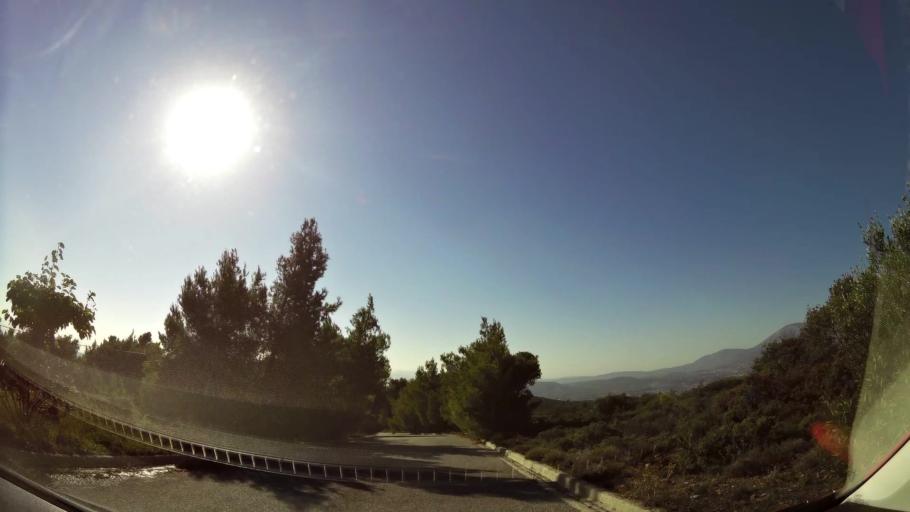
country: GR
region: Attica
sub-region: Nomarchia Anatolikis Attikis
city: Dhrafi
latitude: 38.0296
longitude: 23.8927
